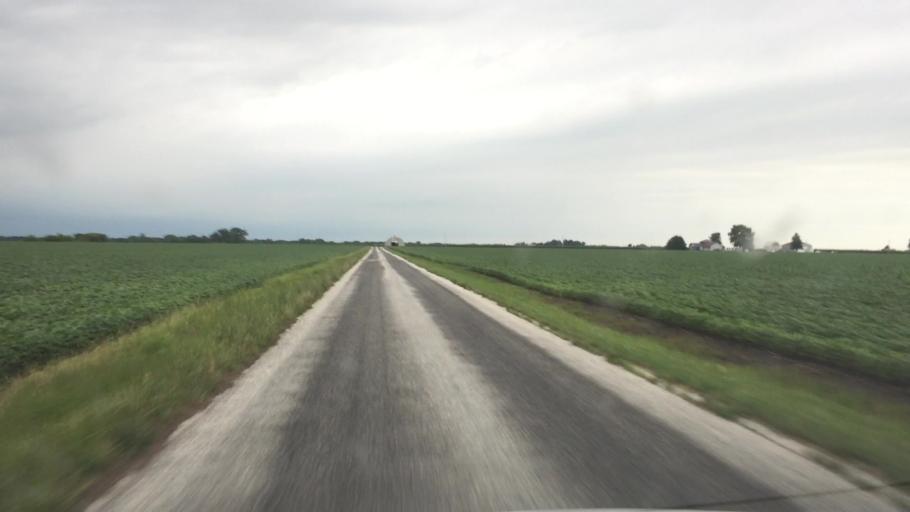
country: US
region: Illinois
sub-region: Adams County
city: Camp Point
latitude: 40.2245
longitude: -90.9691
